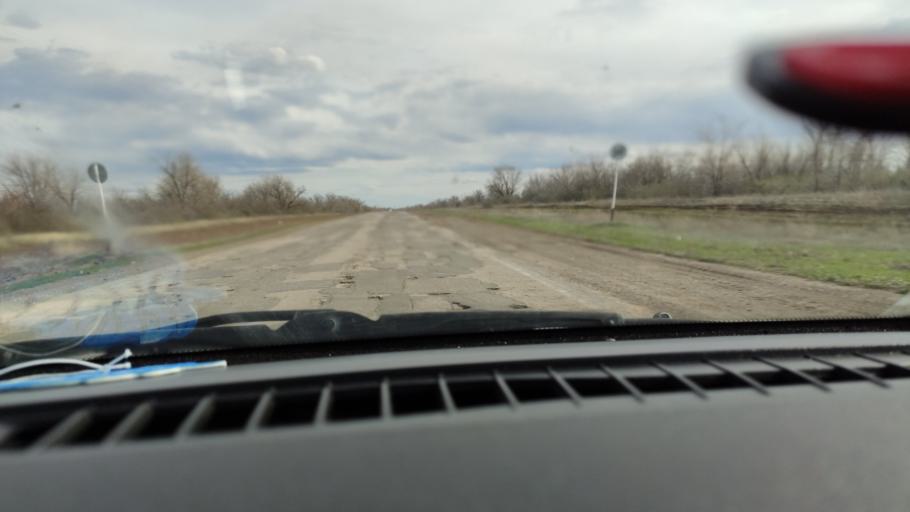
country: RU
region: Saratov
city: Rovnoye
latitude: 50.9516
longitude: 46.1229
